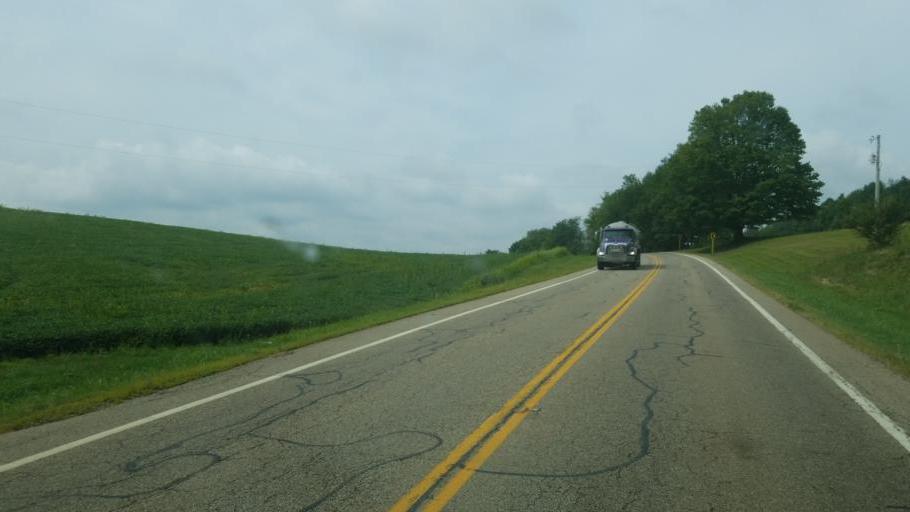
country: US
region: Ohio
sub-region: Knox County
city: Danville
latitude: 40.5046
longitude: -82.3340
